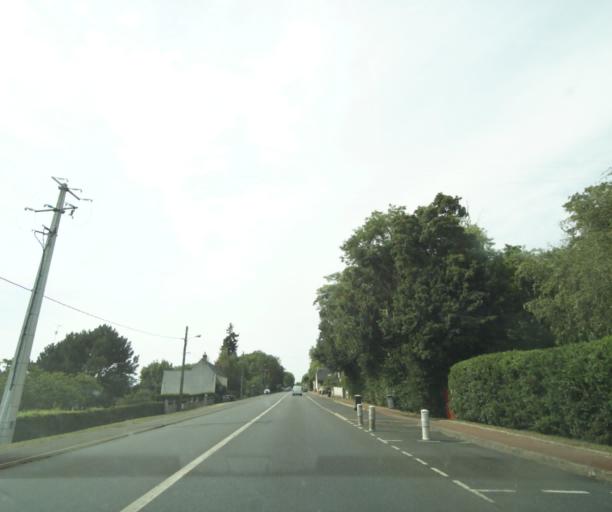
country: FR
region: Centre
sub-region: Departement d'Indre-et-Loire
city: La Membrolle-sur-Choisille
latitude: 47.4422
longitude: 0.6370
